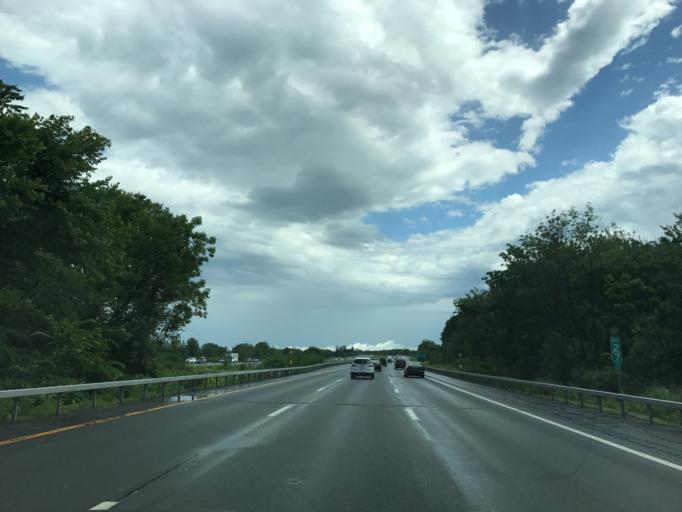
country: US
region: New York
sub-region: Albany County
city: Roessleville
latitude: 42.7240
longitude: -73.8051
